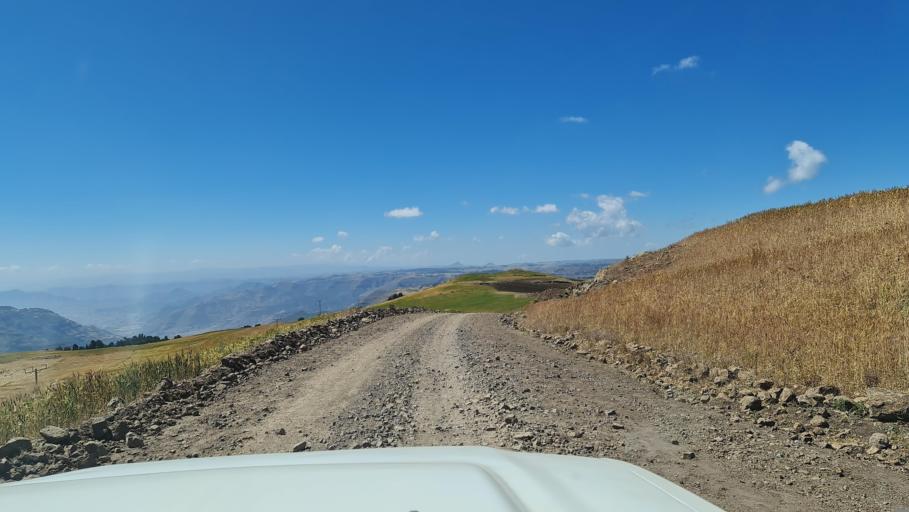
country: ET
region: Amhara
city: Debark'
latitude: 13.2333
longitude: 38.1041
